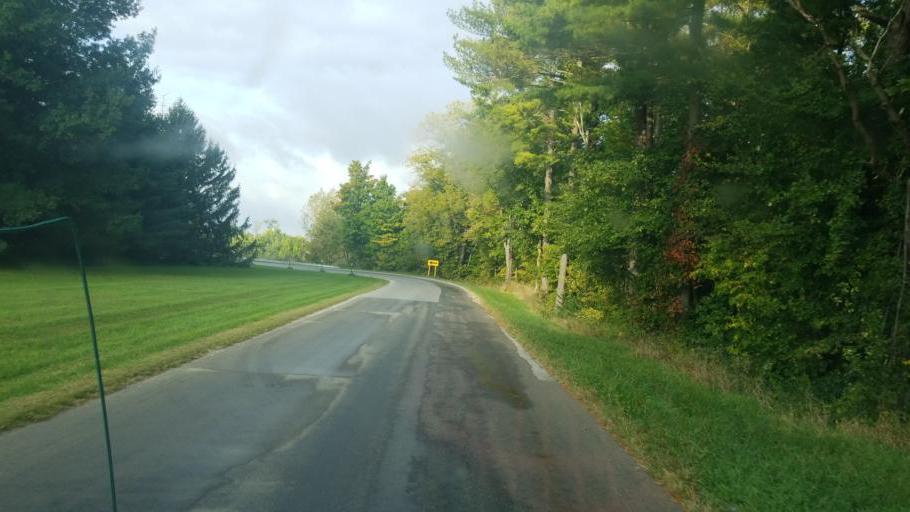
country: US
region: Ohio
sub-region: Wyandot County
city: Upper Sandusky
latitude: 40.8613
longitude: -83.3667
